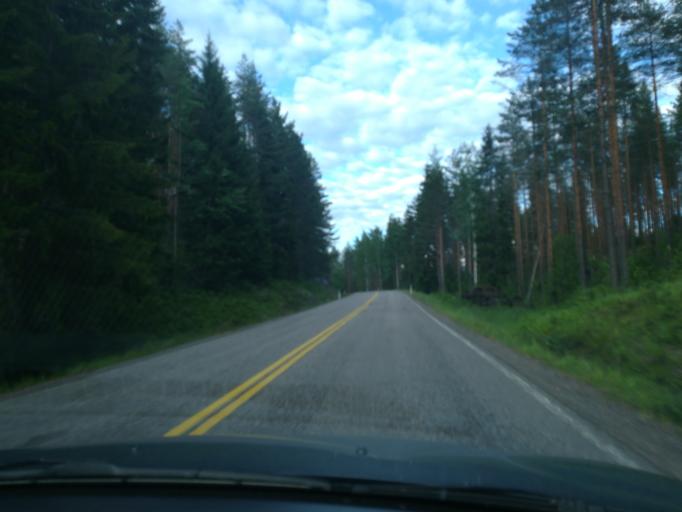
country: FI
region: Southern Savonia
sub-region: Mikkeli
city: Puumala
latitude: 61.5114
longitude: 27.8793
